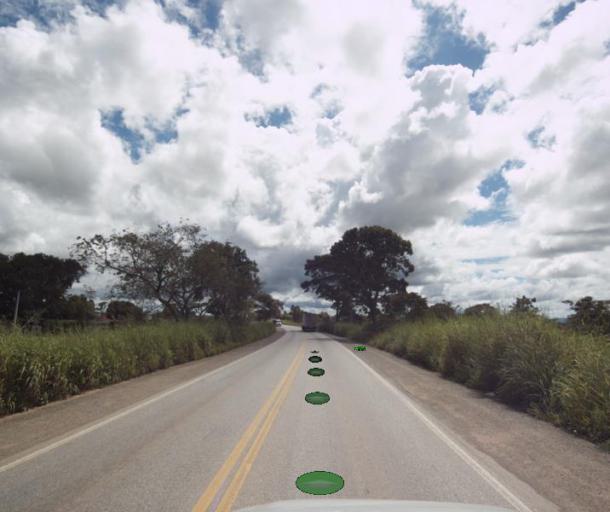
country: BR
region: Goias
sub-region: Uruacu
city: Uruacu
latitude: -14.3060
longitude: -49.1480
